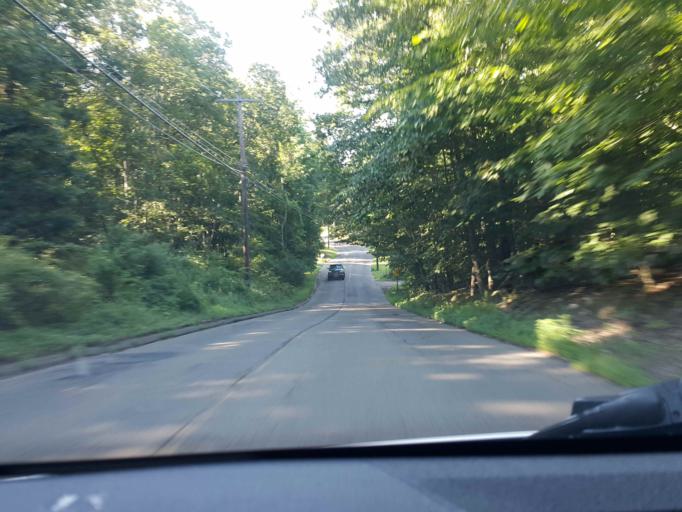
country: US
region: Connecticut
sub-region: New Haven County
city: North Branford
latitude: 41.2786
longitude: -72.7563
